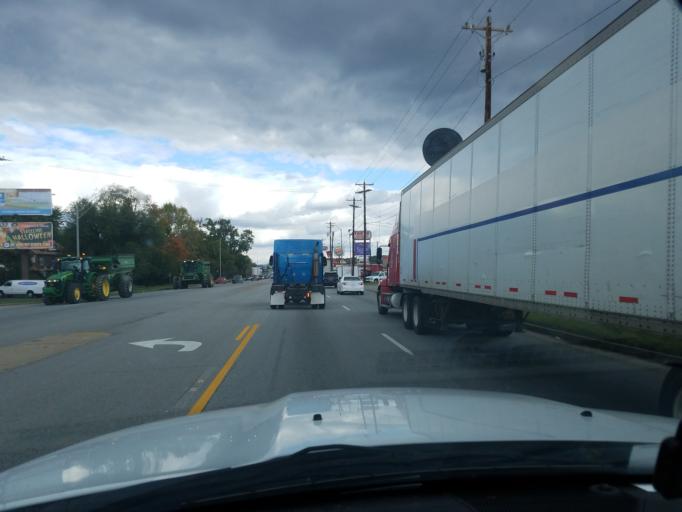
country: US
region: Kentucky
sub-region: Henderson County
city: Henderson
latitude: 37.8683
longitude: -87.5716
